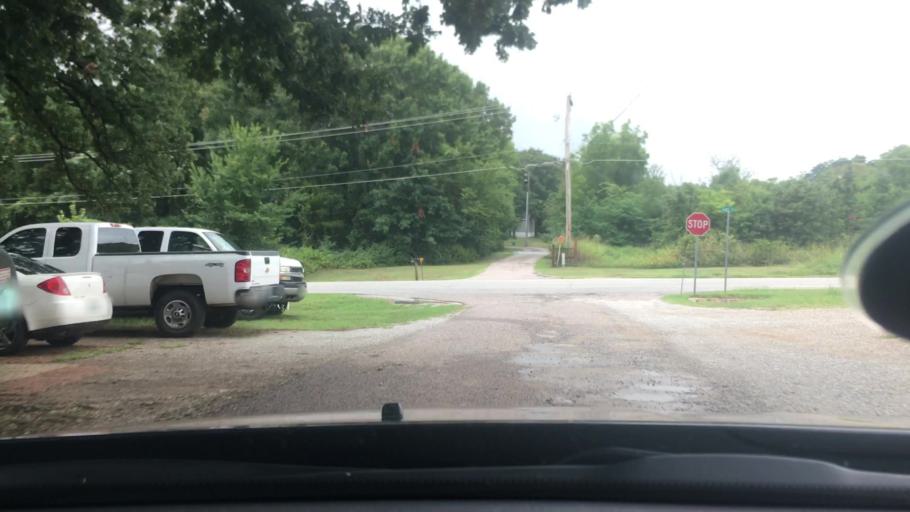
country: US
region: Oklahoma
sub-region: Bryan County
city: Colbert
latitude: 33.8533
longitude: -96.5181
